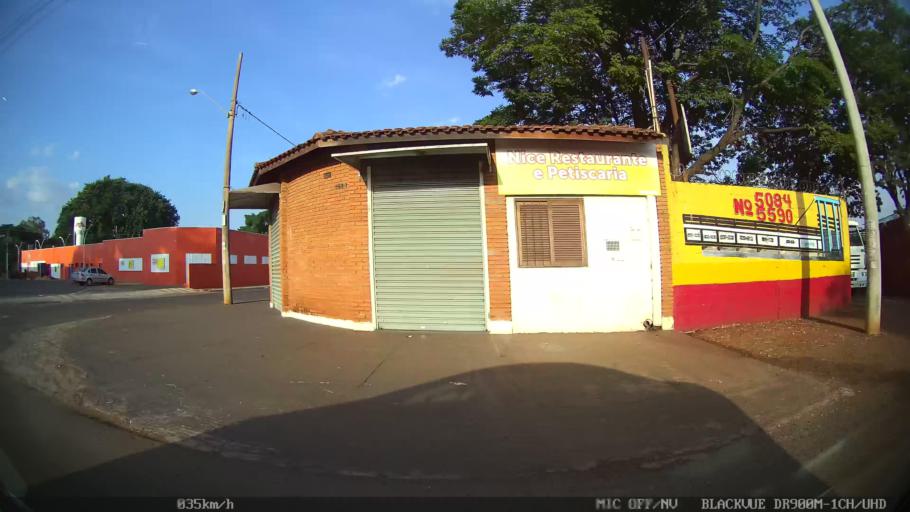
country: BR
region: Sao Paulo
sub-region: Ribeirao Preto
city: Ribeirao Preto
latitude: -21.1274
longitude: -47.7856
